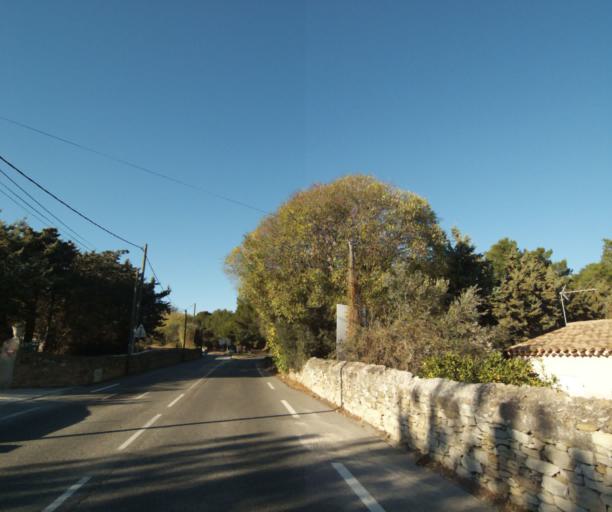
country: FR
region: Provence-Alpes-Cote d'Azur
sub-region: Departement des Bouches-du-Rhone
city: La Ciotat
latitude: 43.1936
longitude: 5.6003
